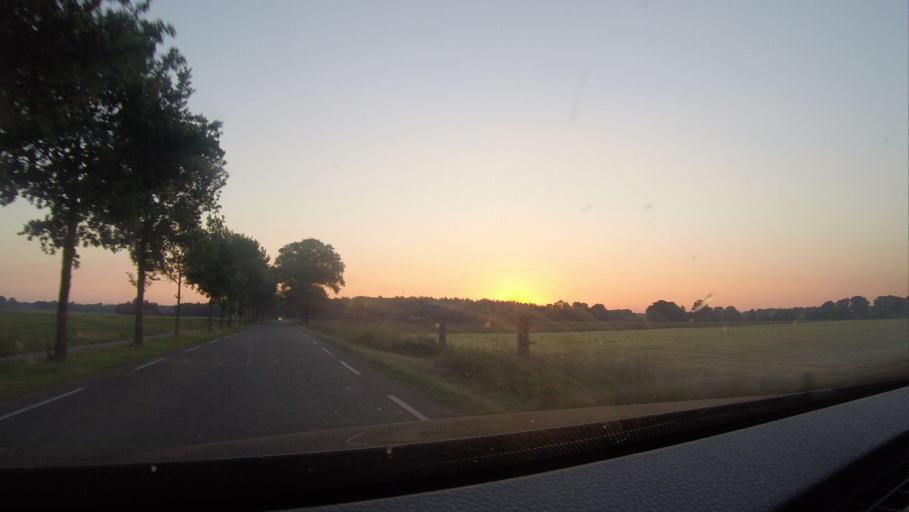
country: NL
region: Overijssel
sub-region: Gemeente Raalte
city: Raalte
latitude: 52.3046
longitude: 6.2707
